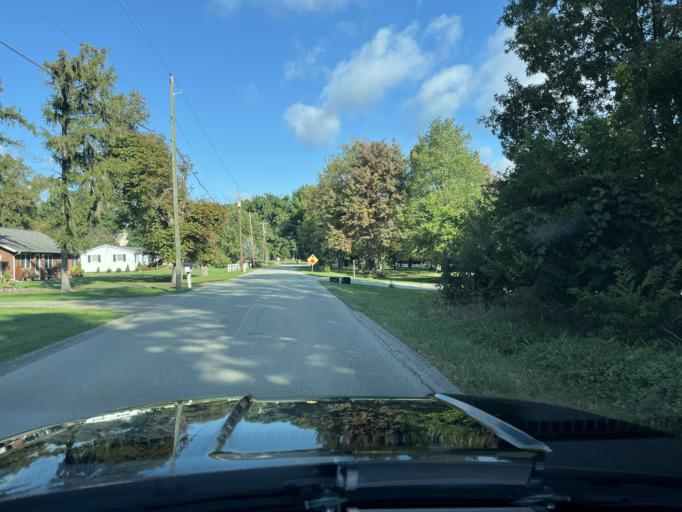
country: US
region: Pennsylvania
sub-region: Fayette County
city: South Uniontown
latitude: 39.8883
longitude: -79.7562
